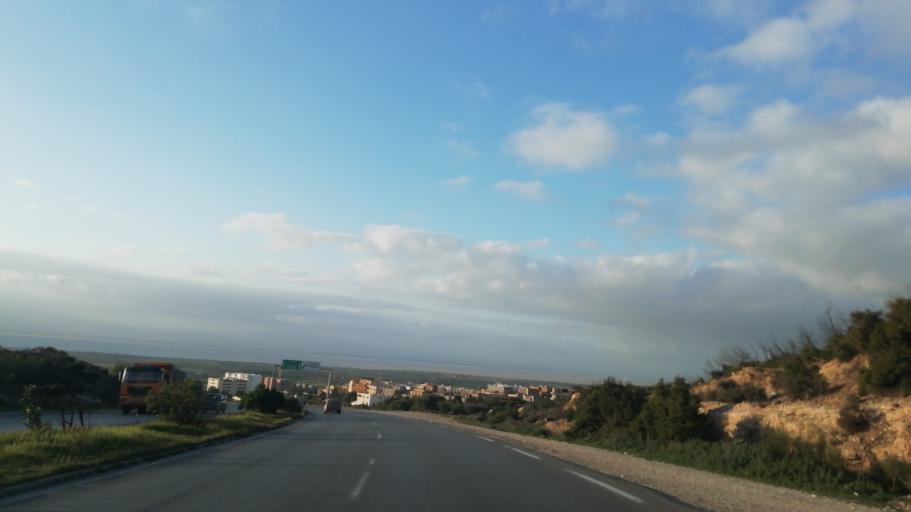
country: DZ
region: Oran
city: Es Senia
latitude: 35.6272
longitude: -0.7186
